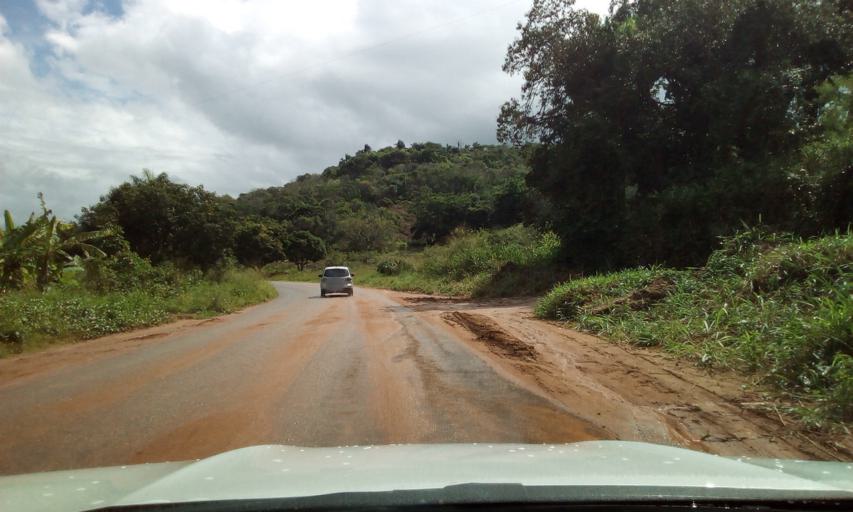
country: BR
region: Paraiba
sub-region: Areia
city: Areia
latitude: -6.9346
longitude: -35.6558
